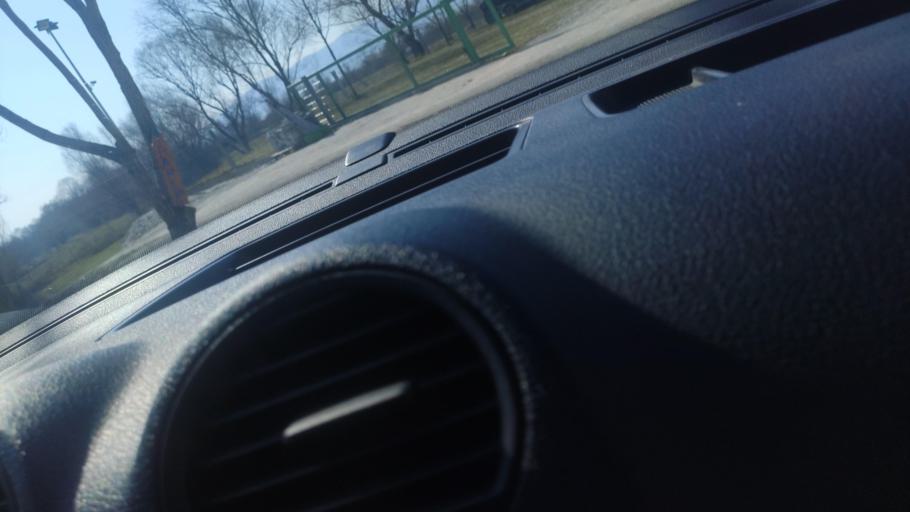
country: AL
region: Shkoder
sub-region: Rrethi i Malesia e Madhe
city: Grude-Fushe
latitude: 42.1567
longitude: 19.4456
